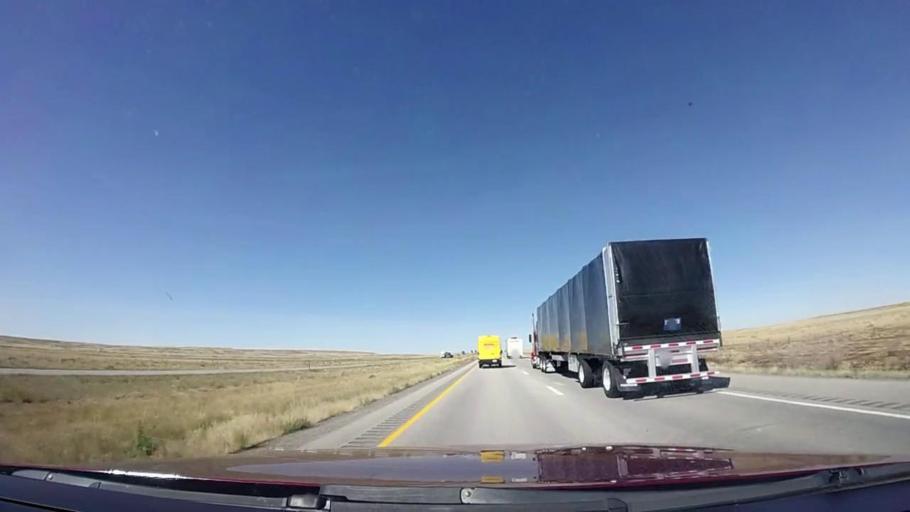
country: US
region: Wyoming
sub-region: Carbon County
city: Rawlins
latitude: 41.6622
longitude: -108.0564
